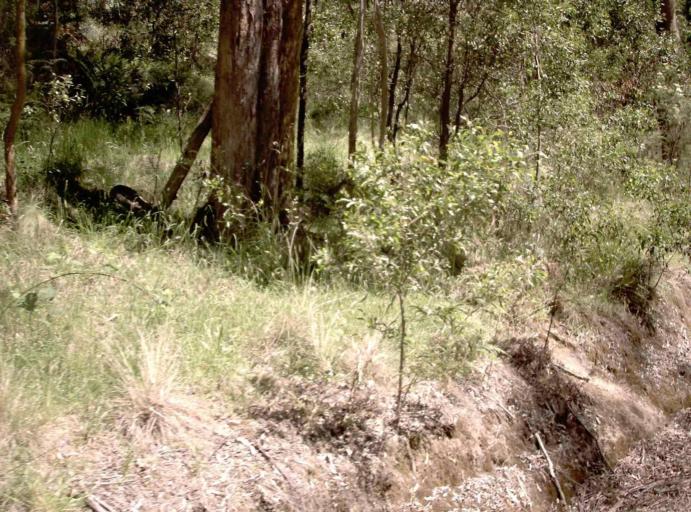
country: AU
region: Victoria
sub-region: East Gippsland
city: Lakes Entrance
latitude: -37.2274
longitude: 148.2632
